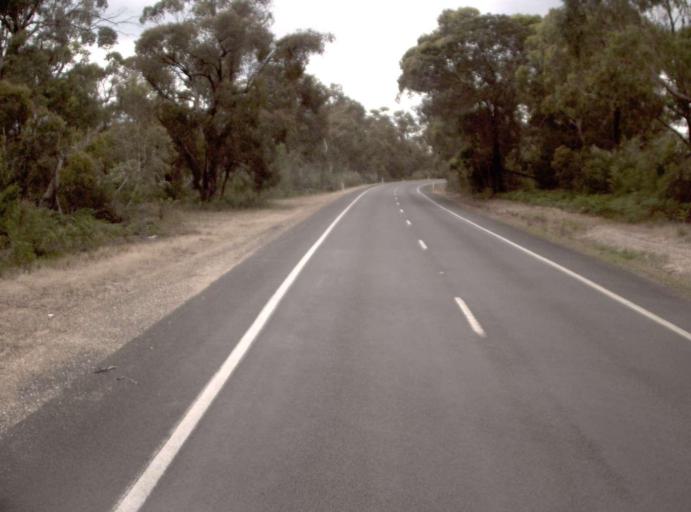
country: AU
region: Victoria
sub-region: Wellington
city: Sale
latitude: -38.2615
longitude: 147.0366
